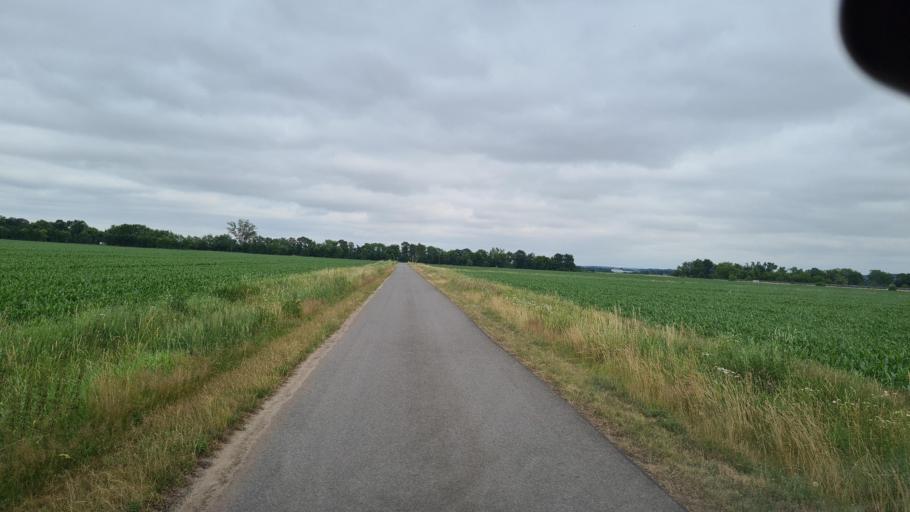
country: DE
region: Brandenburg
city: Groden
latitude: 51.4110
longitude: 13.5825
